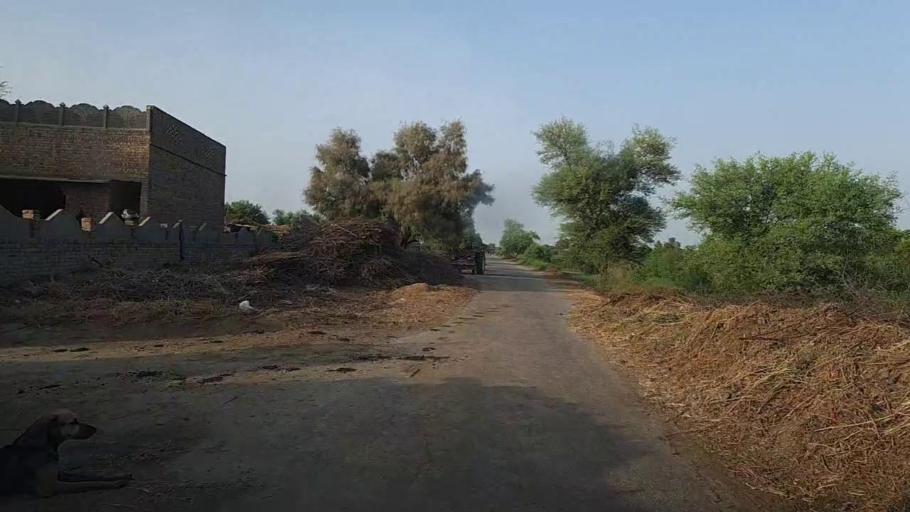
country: PK
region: Sindh
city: Ubauro
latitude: 28.1264
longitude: 69.8301
